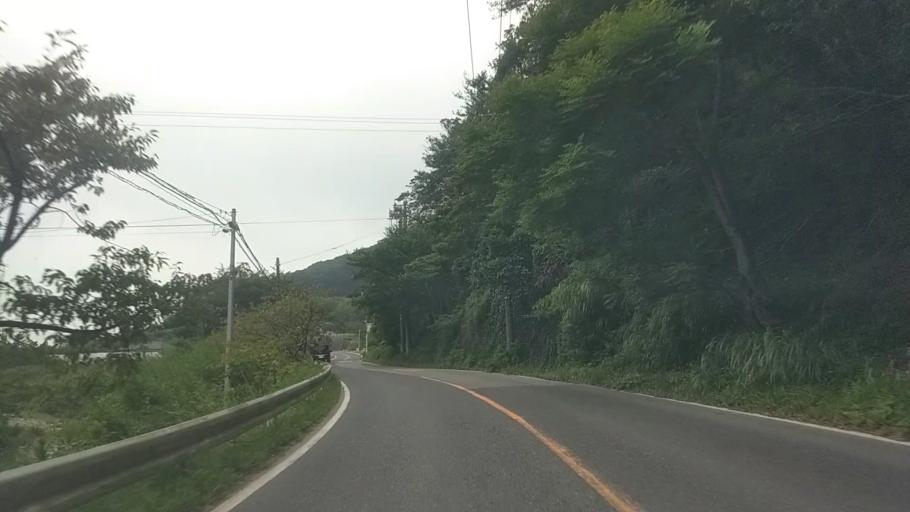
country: JP
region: Chiba
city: Tateyama
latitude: 35.1451
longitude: 139.8620
